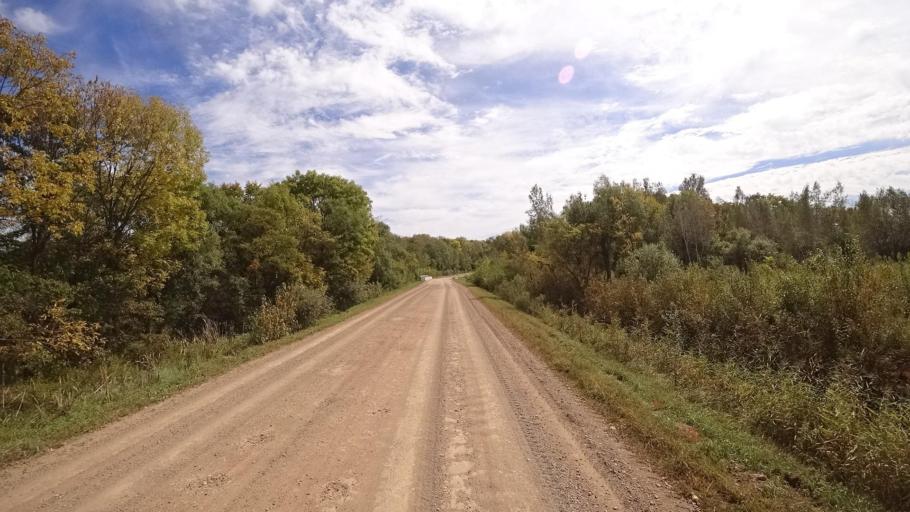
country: RU
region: Primorskiy
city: Yakovlevka
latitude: 44.6356
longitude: 133.5987
